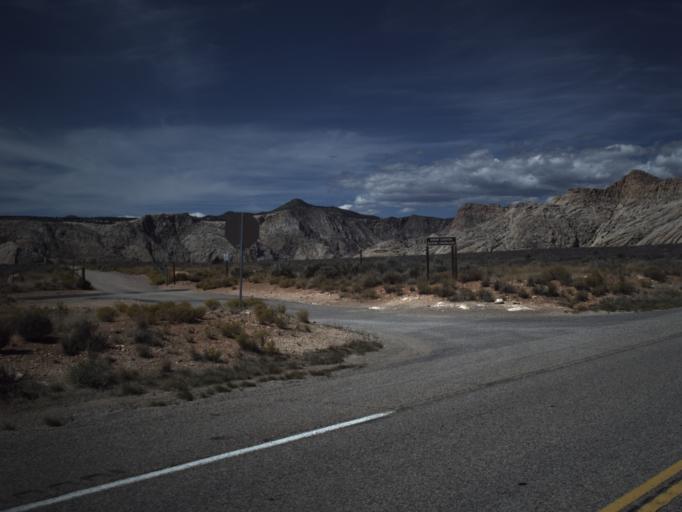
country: US
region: Utah
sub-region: Washington County
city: Ivins
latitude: 37.2178
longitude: -113.6332
